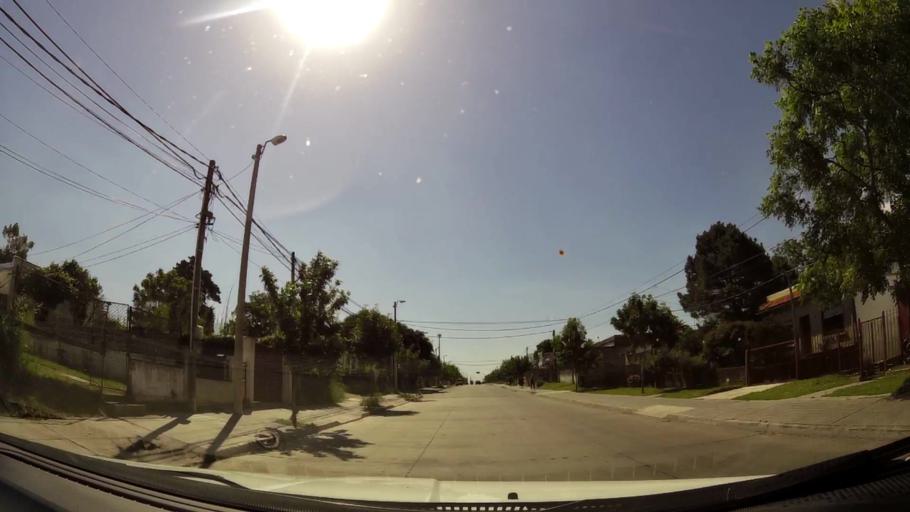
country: UY
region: Canelones
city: La Paz
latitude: -34.8391
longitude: -56.2483
